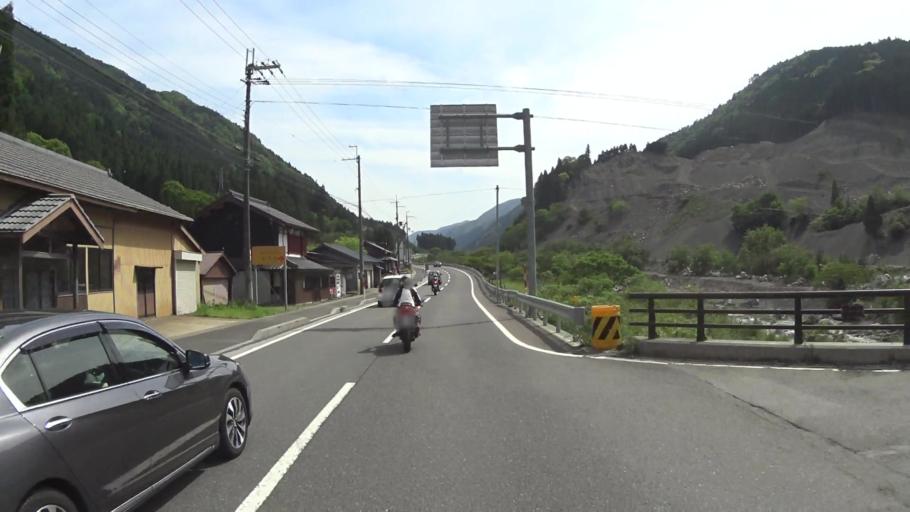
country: JP
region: Shiga Prefecture
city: Kitahama
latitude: 35.2643
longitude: 135.8743
